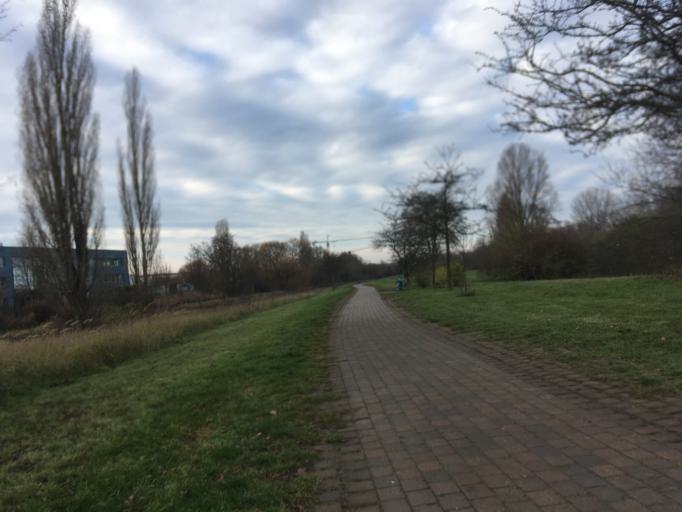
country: DE
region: Berlin
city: Falkenberg
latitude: 52.5676
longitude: 13.5403
